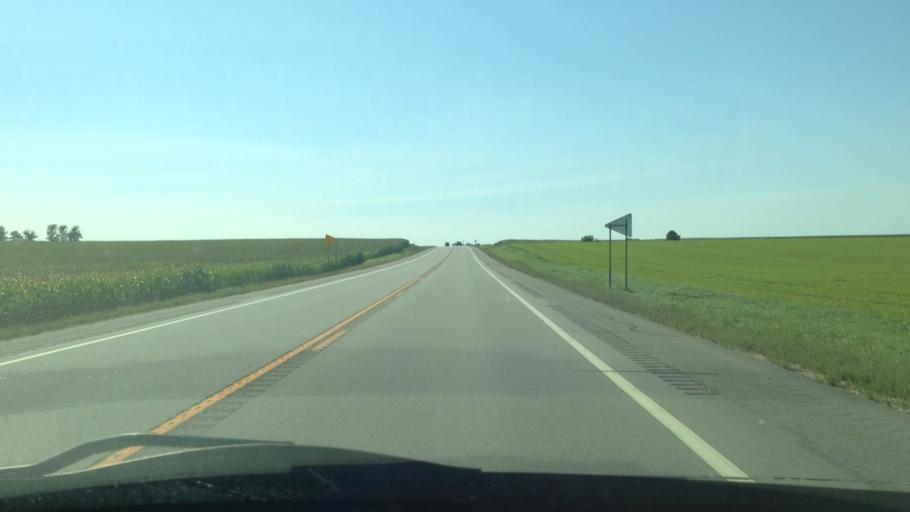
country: US
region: Minnesota
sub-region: Olmsted County
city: Eyota
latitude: 43.9993
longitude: -92.2700
